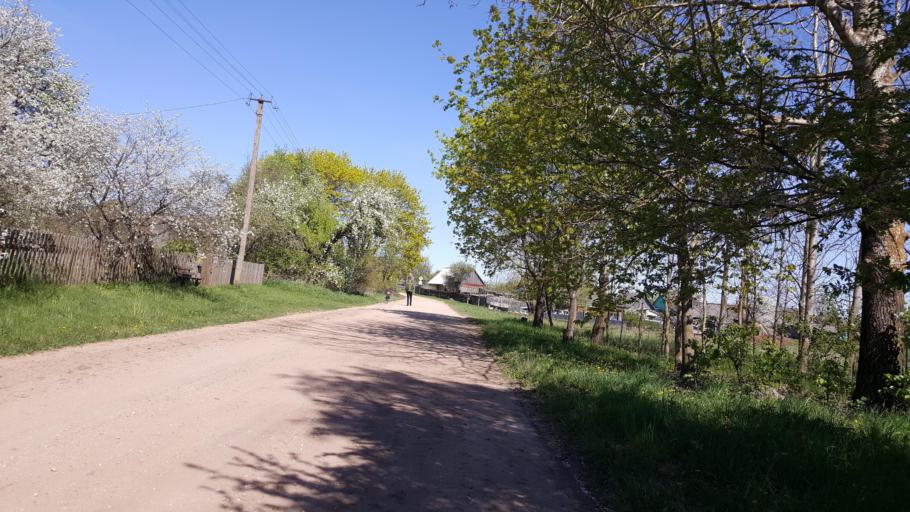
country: BY
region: Brest
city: Kamyanyets
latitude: 52.4554
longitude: 23.8766
